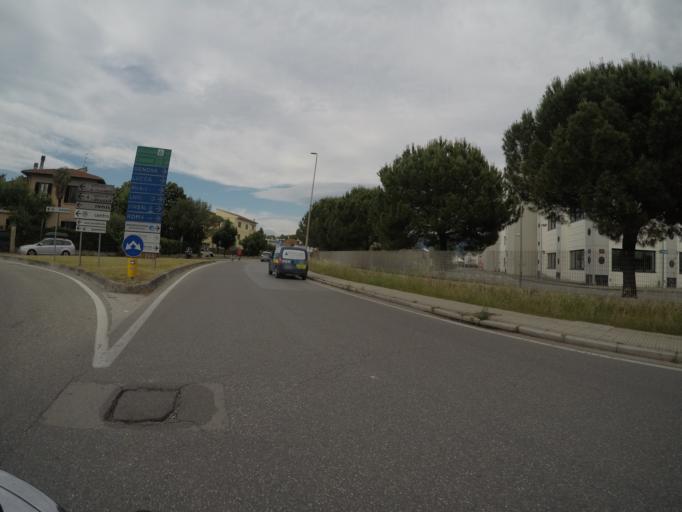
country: IT
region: Tuscany
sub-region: Province of Pisa
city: Pisa
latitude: 43.7191
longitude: 10.4201
